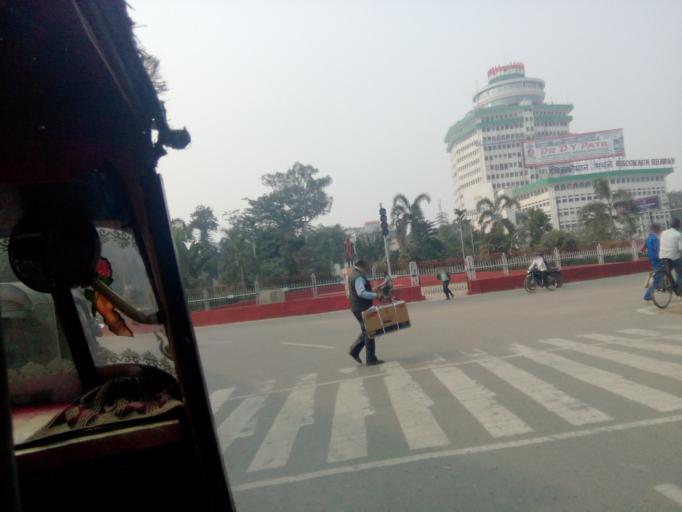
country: IN
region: Bihar
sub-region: Patna
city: Patna
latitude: 25.6162
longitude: 85.1425
